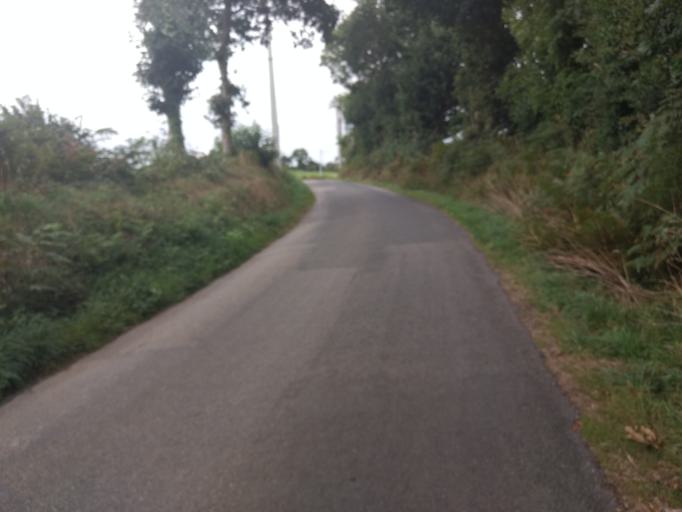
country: FR
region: Brittany
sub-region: Departement du Finistere
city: Loperhet
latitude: 48.3684
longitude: -4.2982
